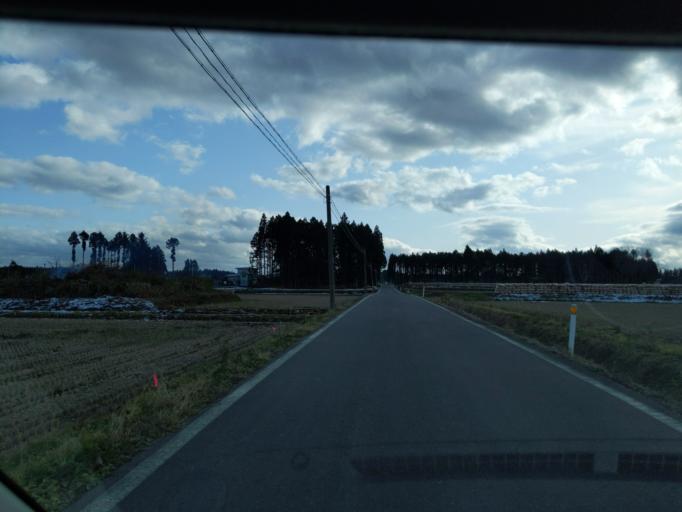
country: JP
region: Iwate
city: Mizusawa
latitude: 39.1253
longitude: 141.0814
